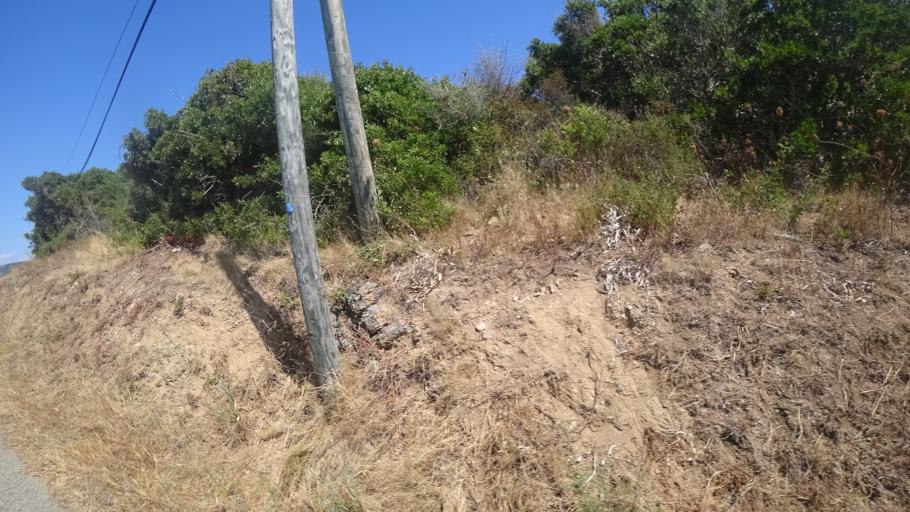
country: FR
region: Corsica
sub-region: Departement de la Corse-du-Sud
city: Alata
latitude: 41.9813
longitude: 8.6756
